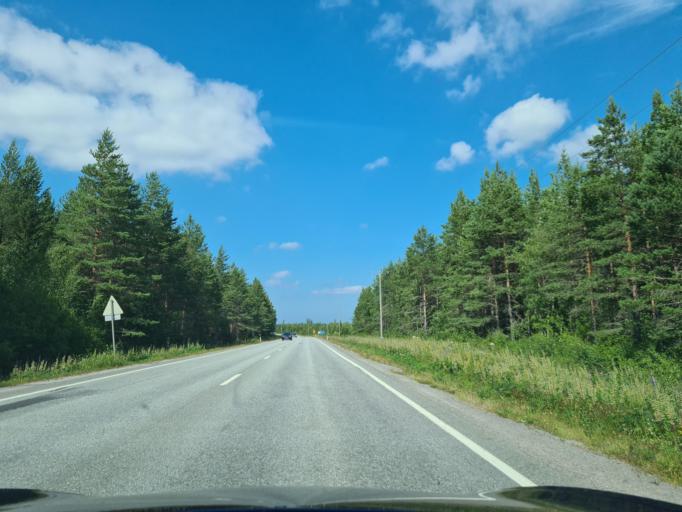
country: FI
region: Ostrobothnia
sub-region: Vaasa
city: Vaasa
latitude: 63.1618
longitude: 21.5915
